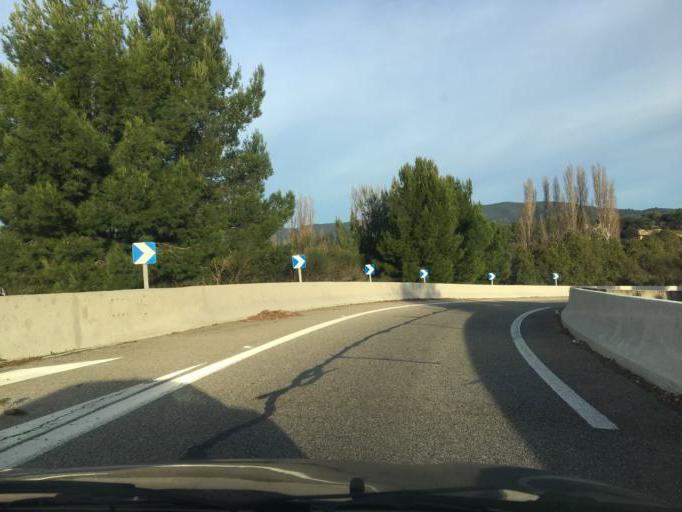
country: FR
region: Provence-Alpes-Cote d'Azur
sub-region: Departement du Vaucluse
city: Lauris
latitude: 43.7374
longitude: 5.3403
